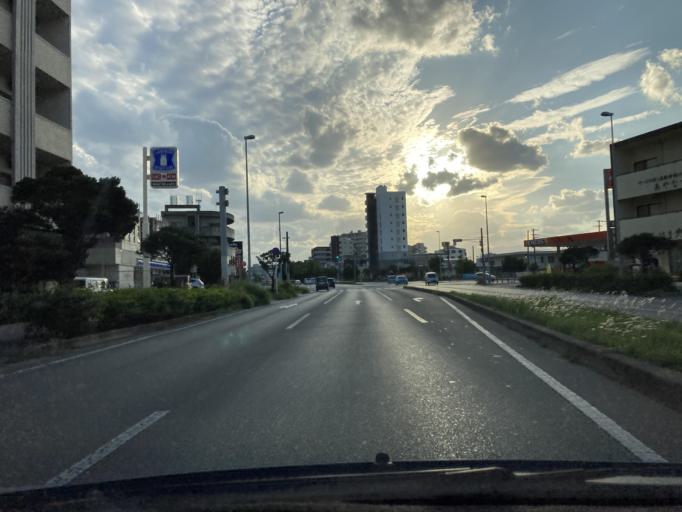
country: JP
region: Okinawa
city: Chatan
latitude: 26.2907
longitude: 127.7559
